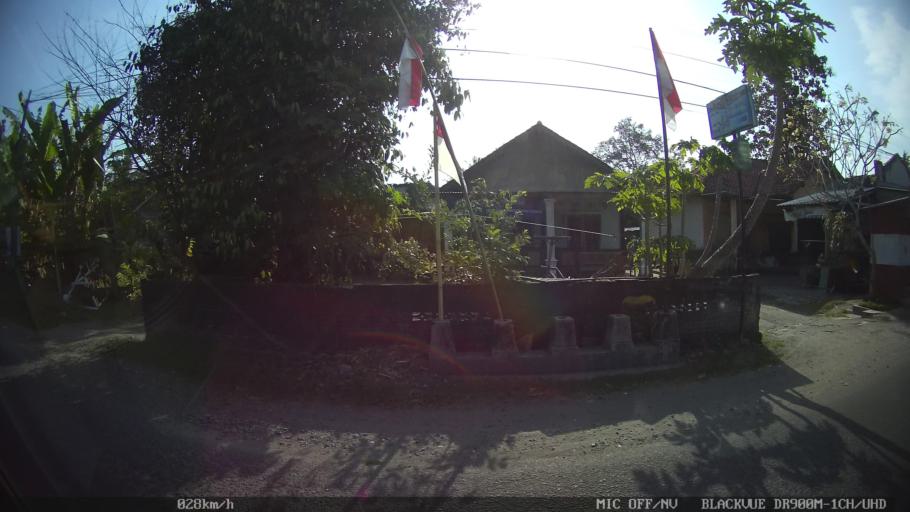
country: ID
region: Daerah Istimewa Yogyakarta
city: Pandak
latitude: -7.8938
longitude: 110.2994
